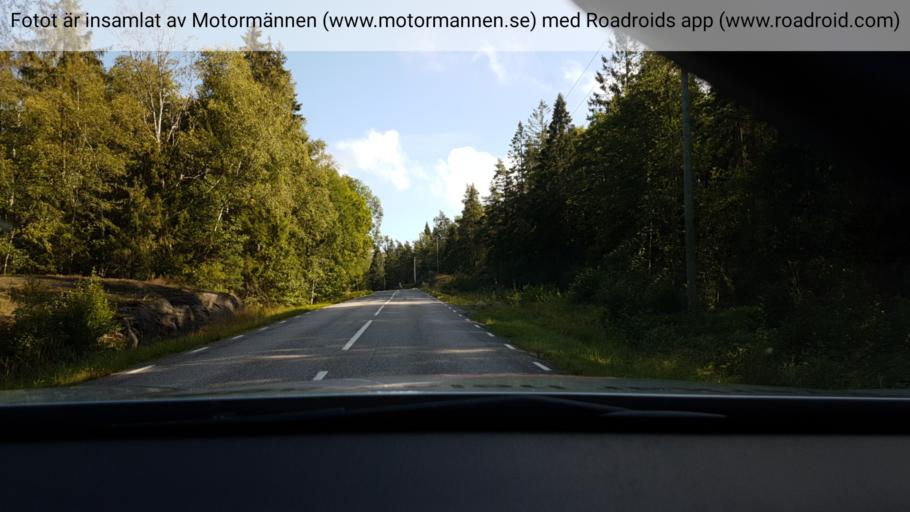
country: SE
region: Stockholm
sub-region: Nynashamns Kommun
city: Osmo
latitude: 58.9353
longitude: 17.7951
